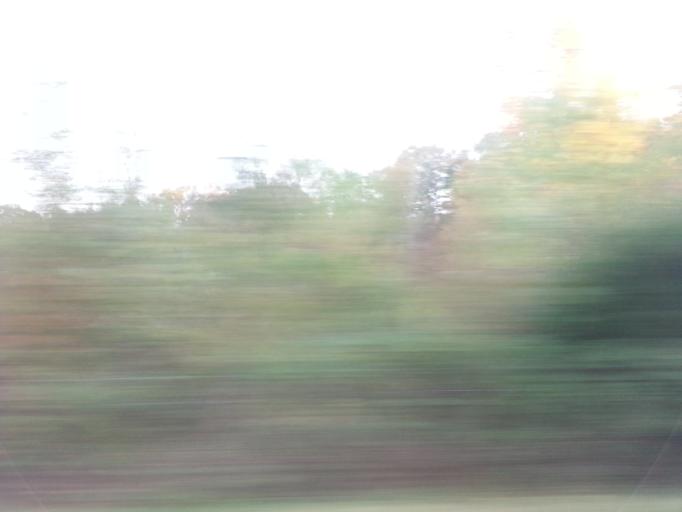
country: US
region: Tennessee
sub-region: Sevier County
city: Seymour
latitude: 35.7878
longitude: -83.7544
